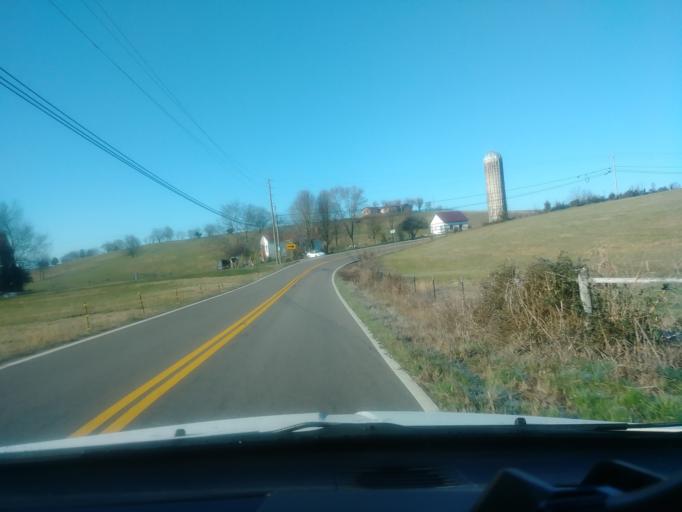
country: US
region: Tennessee
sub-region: Greene County
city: Mosheim
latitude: 36.1139
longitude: -82.9491
